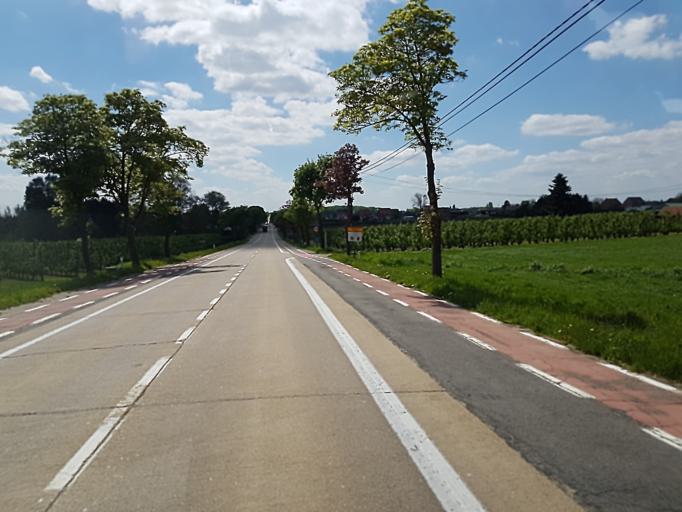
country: BE
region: Flanders
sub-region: Provincie Vlaams-Brabant
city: Glabbeek-Zuurbemde
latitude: 50.8988
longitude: 4.9728
